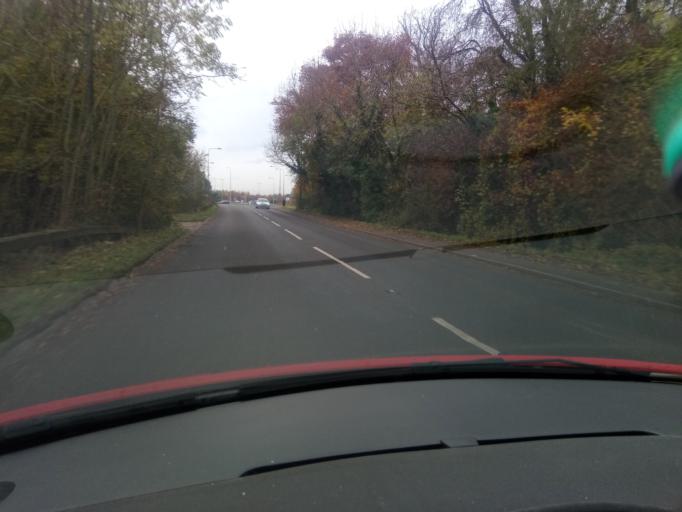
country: GB
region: England
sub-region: Derbyshire
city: Borrowash
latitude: 52.8833
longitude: -1.4013
